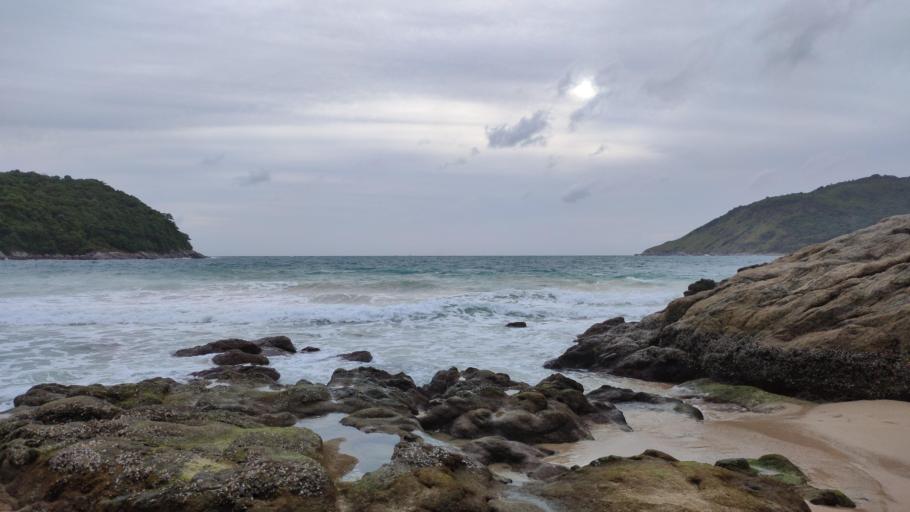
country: TH
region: Phuket
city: Nai Harn
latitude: 7.7682
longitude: 98.3063
